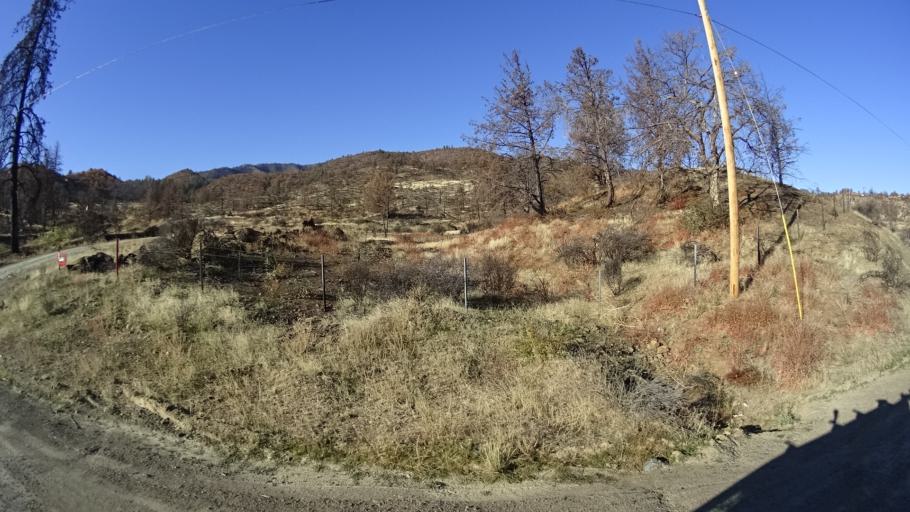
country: US
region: California
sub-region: Siskiyou County
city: Montague
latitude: 41.8984
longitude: -122.5671
